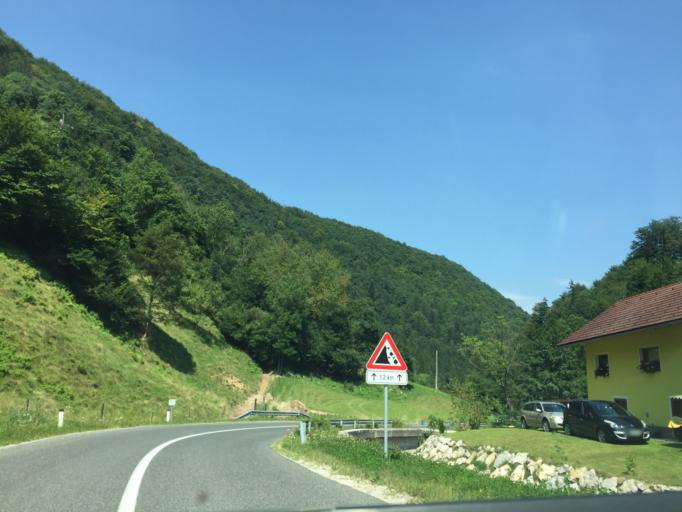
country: SI
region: Prebold
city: Prebold
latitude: 46.2093
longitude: 15.0894
